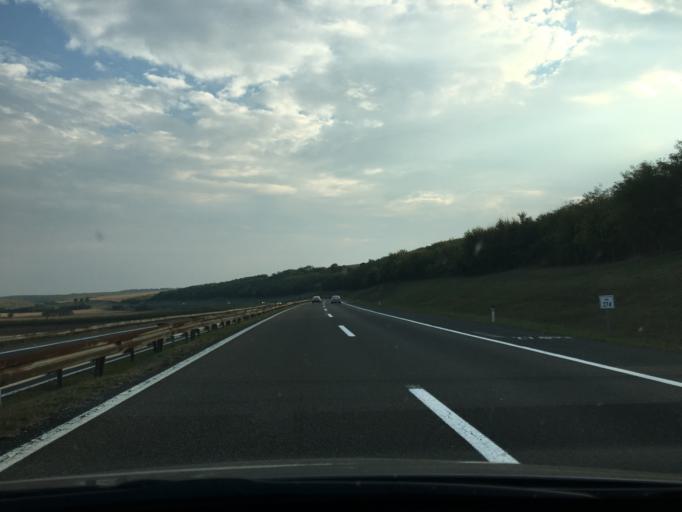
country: RS
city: Lugavcina
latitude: 44.4984
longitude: 21.0231
